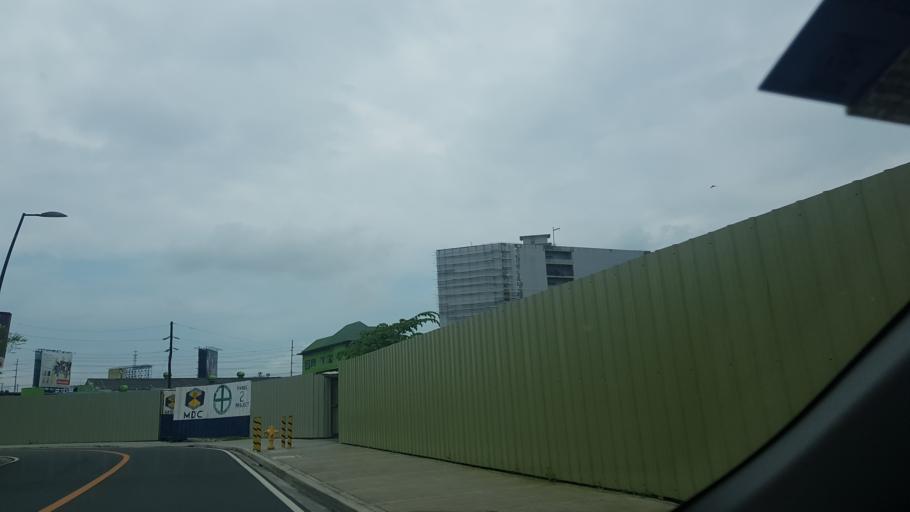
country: PH
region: Calabarzon
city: Del Monte
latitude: 14.6549
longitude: 121.0034
